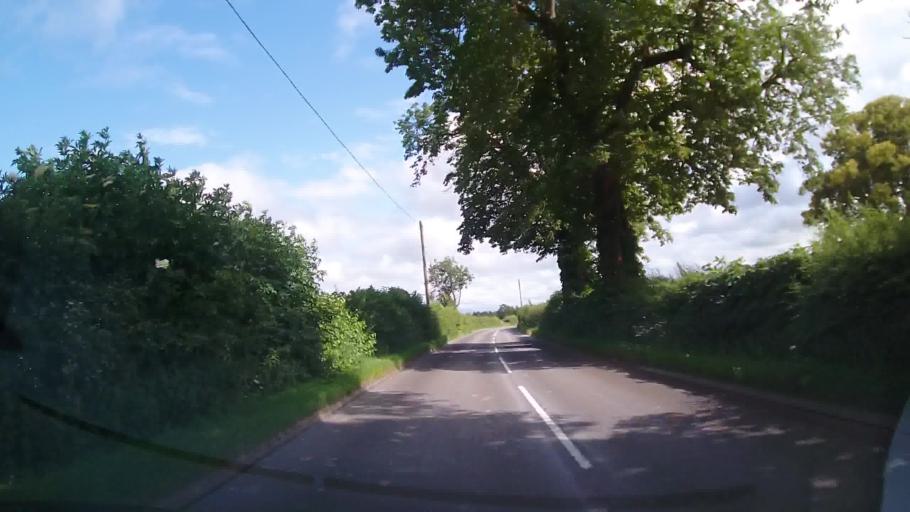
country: GB
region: England
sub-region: Shropshire
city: Pant
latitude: 52.8071
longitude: -3.0279
